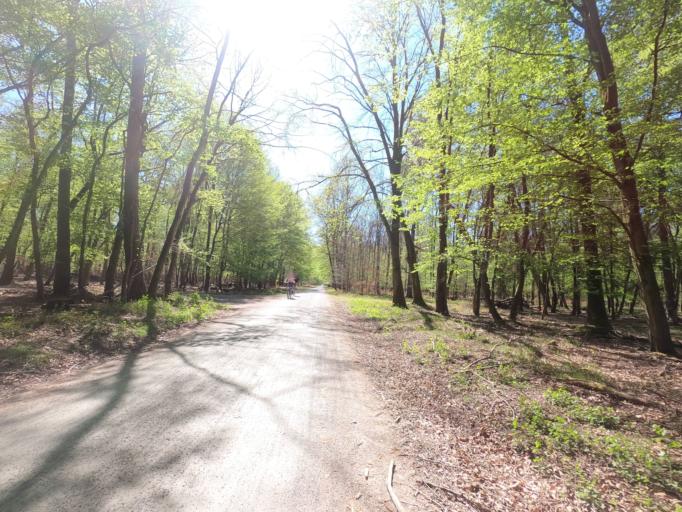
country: DE
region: Hesse
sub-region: Regierungsbezirk Darmstadt
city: Nauheim
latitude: 49.9589
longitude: 8.5038
